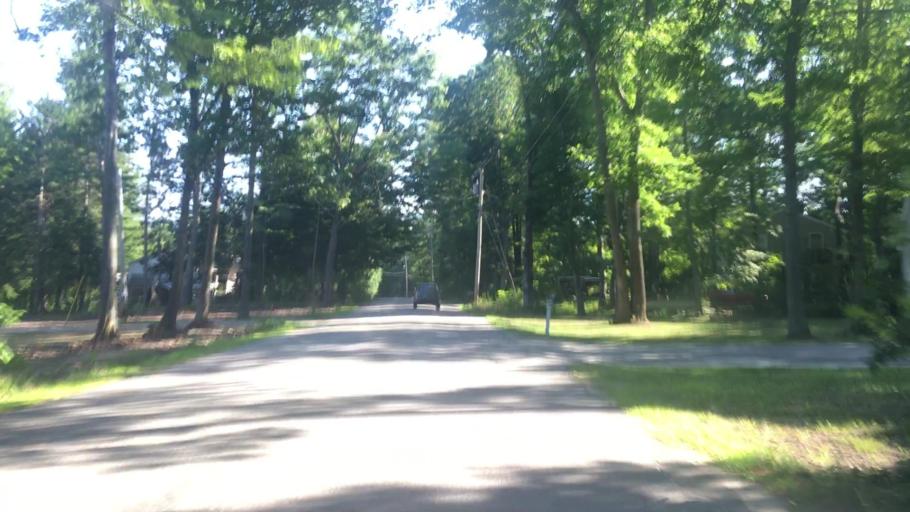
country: US
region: Maine
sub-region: York County
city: Buxton
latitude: 43.7158
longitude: -70.5166
